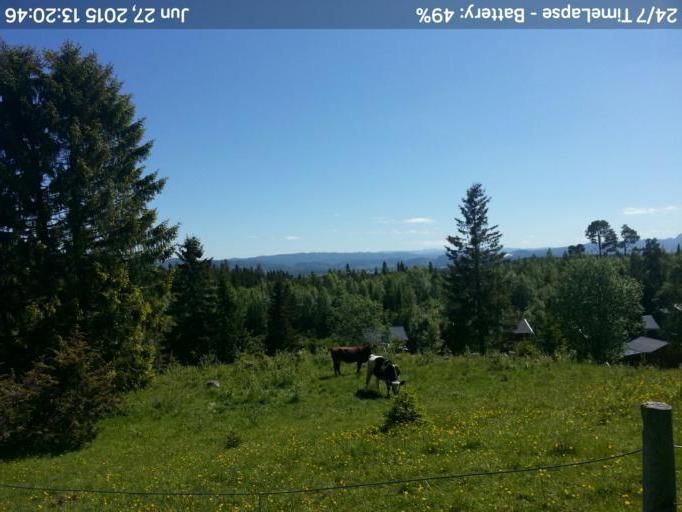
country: NO
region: Sor-Trondelag
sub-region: Trondheim
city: Trondheim
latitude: 63.3993
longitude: 10.3097
